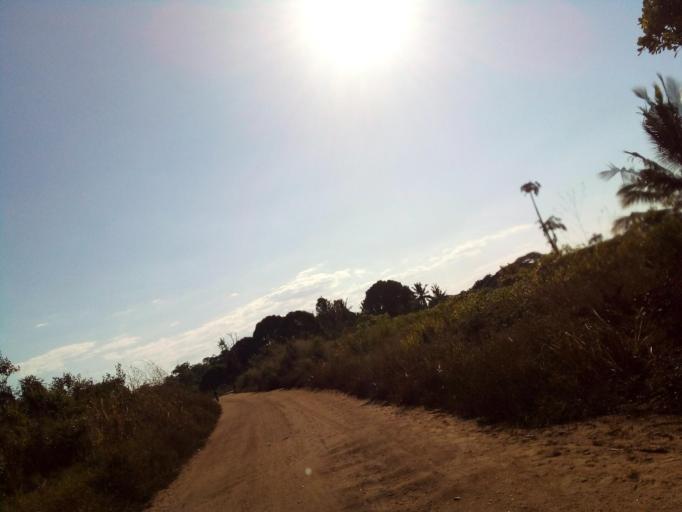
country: MZ
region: Zambezia
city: Quelimane
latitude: -17.4894
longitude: 36.5629
